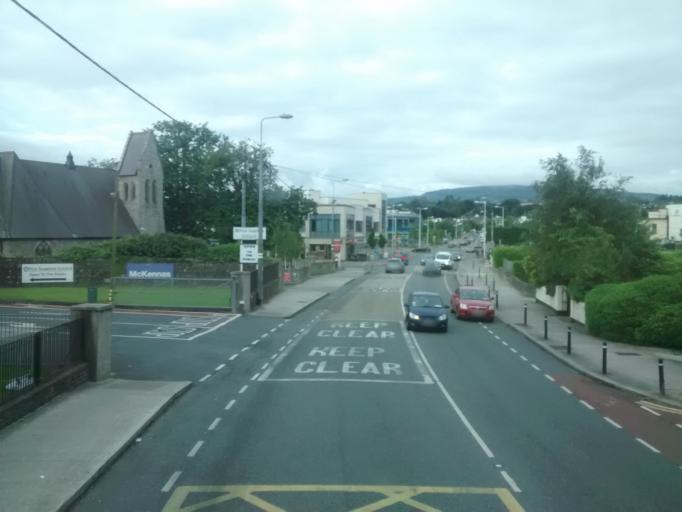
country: IE
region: Leinster
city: Cabinteely
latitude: 53.2793
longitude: -6.1622
